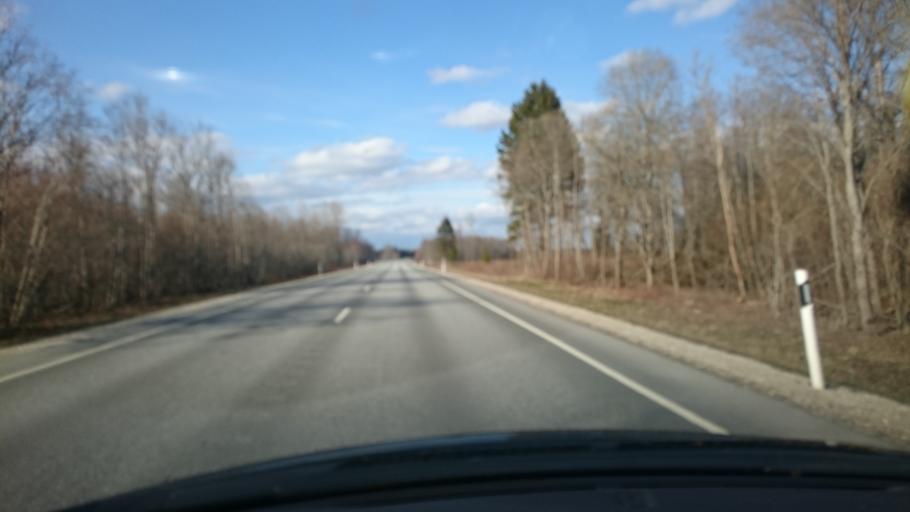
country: EE
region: Laeaene
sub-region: Lihula vald
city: Lihula
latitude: 58.8035
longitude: 24.0482
